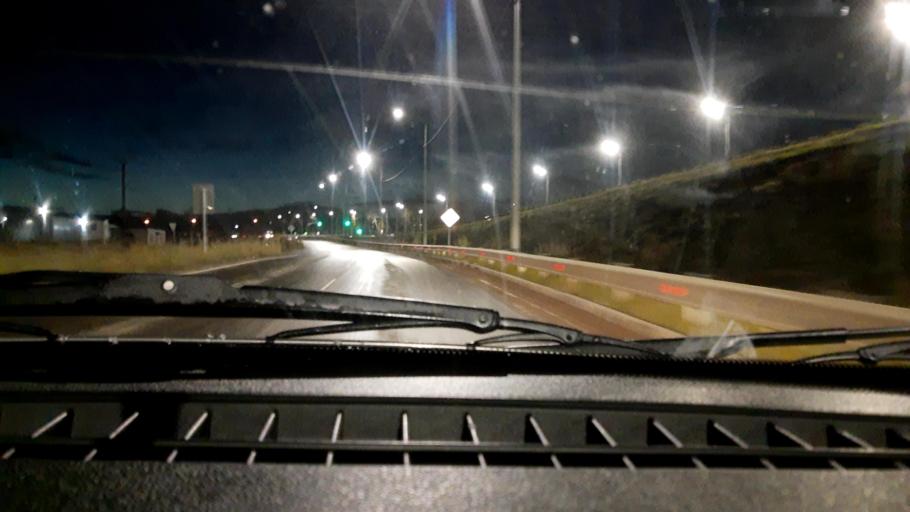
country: RU
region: Bashkortostan
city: Ufa
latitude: 54.8280
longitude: 56.1234
